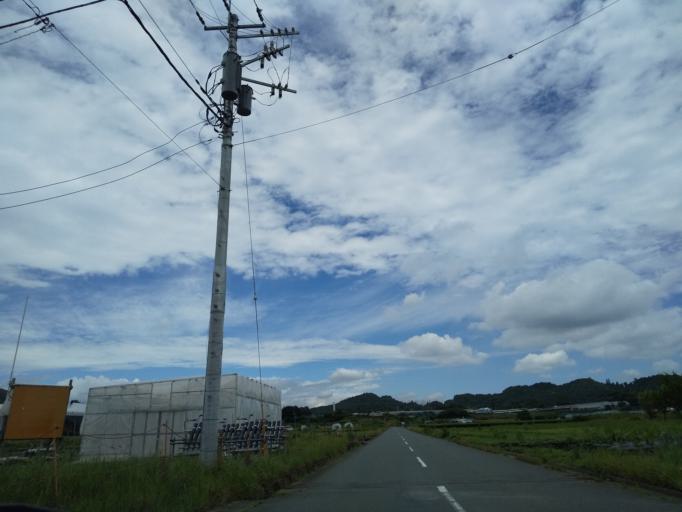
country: JP
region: Kanagawa
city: Zama
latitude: 35.5300
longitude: 139.3023
